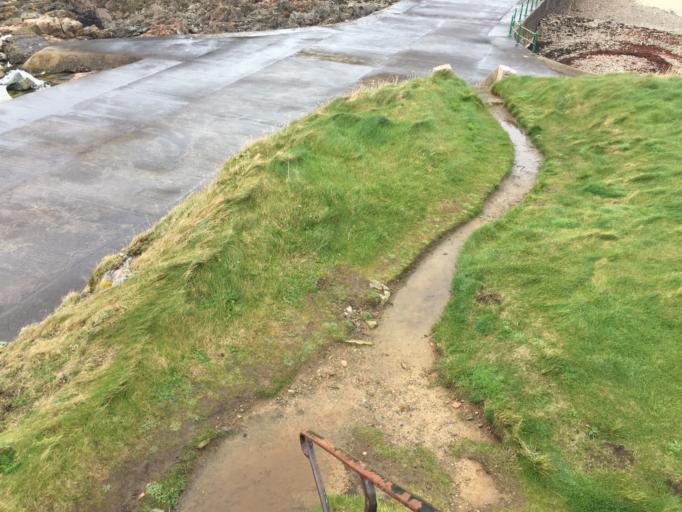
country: JE
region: St Helier
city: Saint Helier
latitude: 49.1735
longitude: -2.1248
